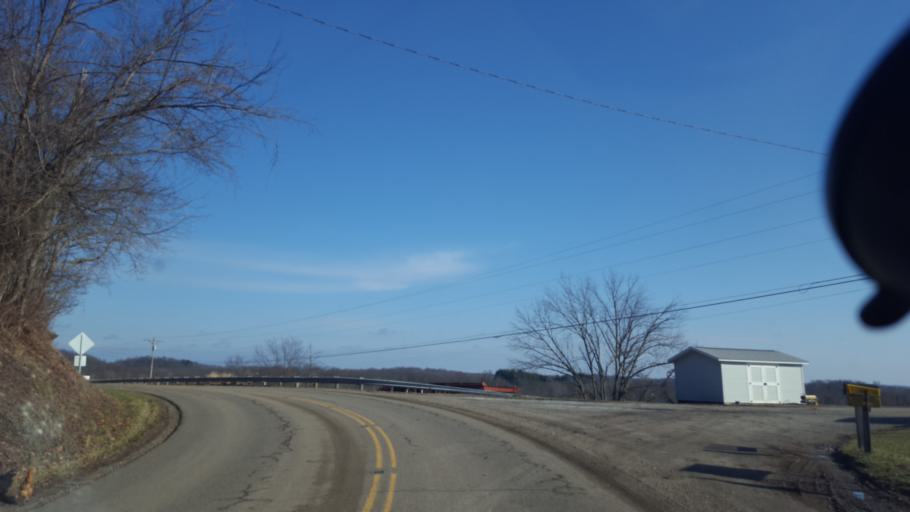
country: US
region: Ohio
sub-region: Tuscarawas County
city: Newcomerstown
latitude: 40.1896
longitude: -81.5269
